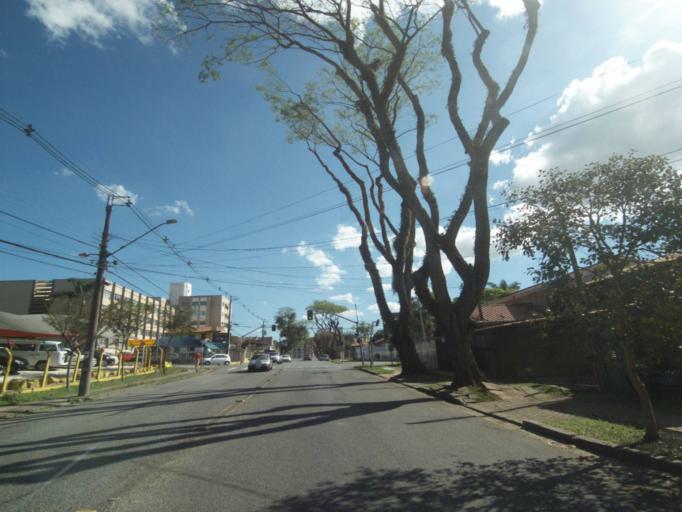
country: BR
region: Parana
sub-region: Curitiba
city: Curitiba
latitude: -25.3972
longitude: -49.2504
